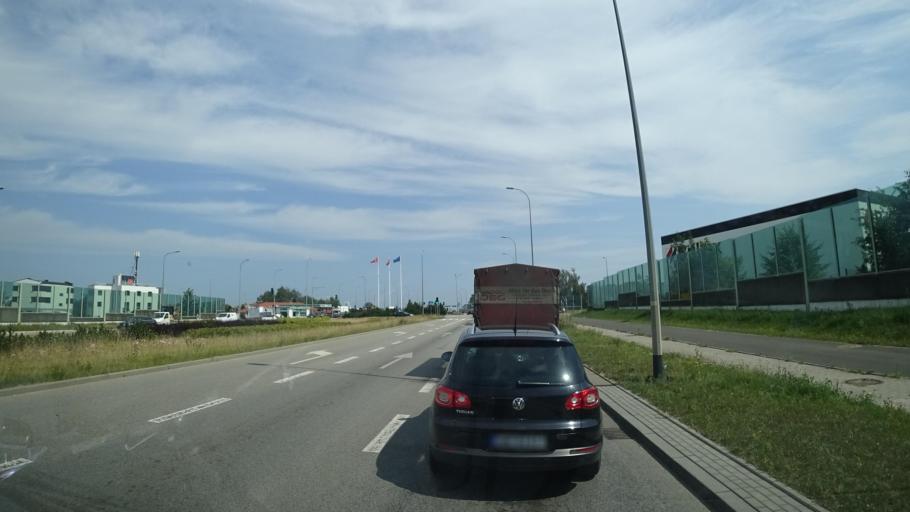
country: PL
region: Pomeranian Voivodeship
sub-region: Powiat gdanski
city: Lublewo Gdanskie
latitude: 54.3500
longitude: 18.5094
